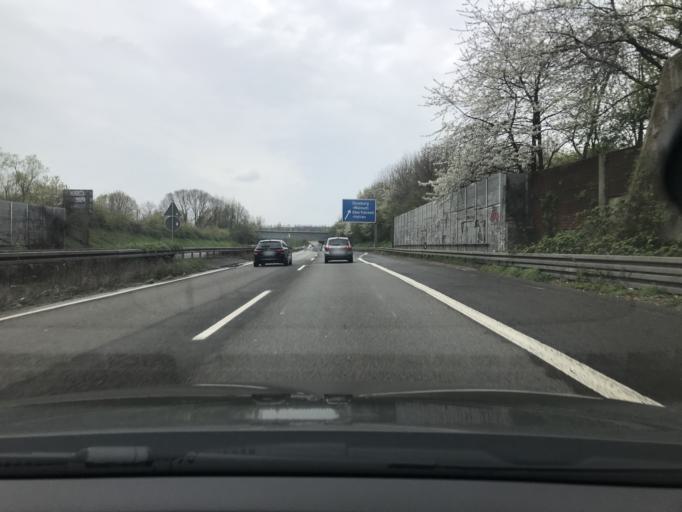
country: DE
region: North Rhine-Westphalia
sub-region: Regierungsbezirk Dusseldorf
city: Dinslaken
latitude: 51.5224
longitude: 6.7600
